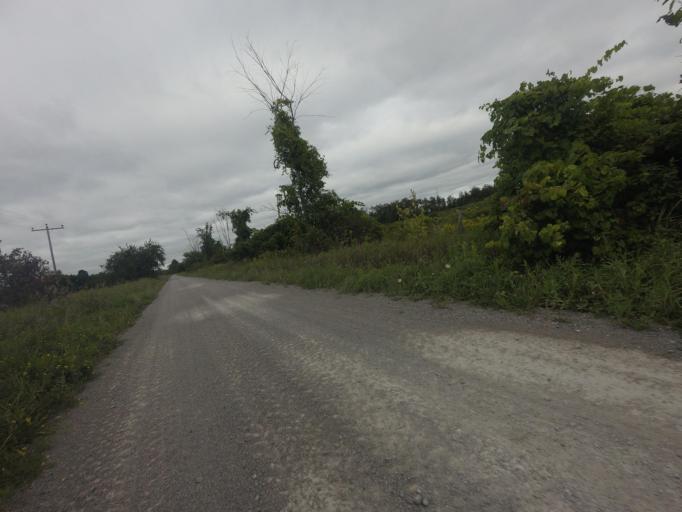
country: CA
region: Ontario
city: Omemee
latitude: 44.4589
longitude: -78.7596
